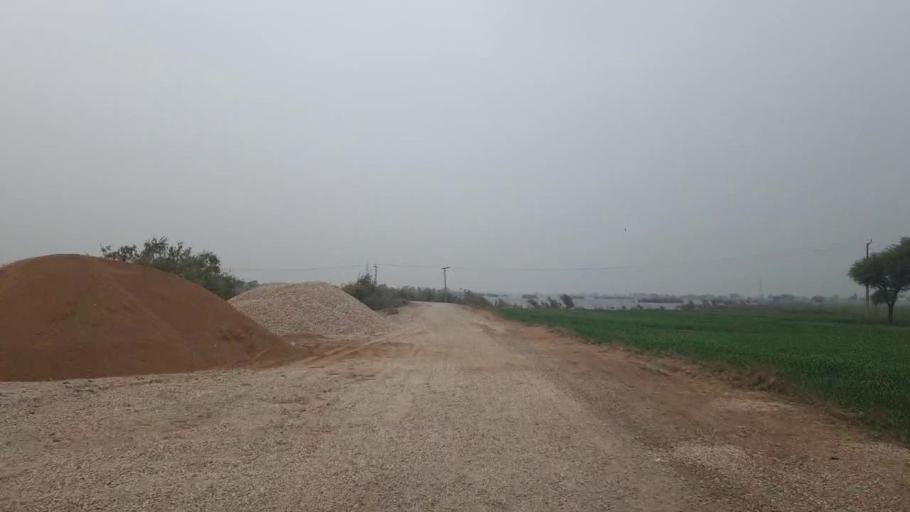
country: PK
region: Sindh
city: Shahdadpur
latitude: 25.8667
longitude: 68.6263
